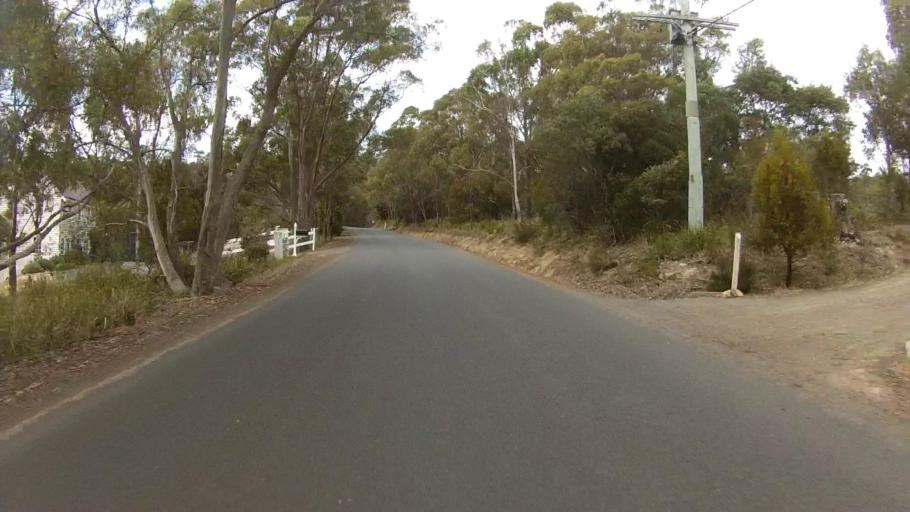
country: AU
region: Tasmania
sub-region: Kingborough
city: Blackmans Bay
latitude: -43.0232
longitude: 147.3075
